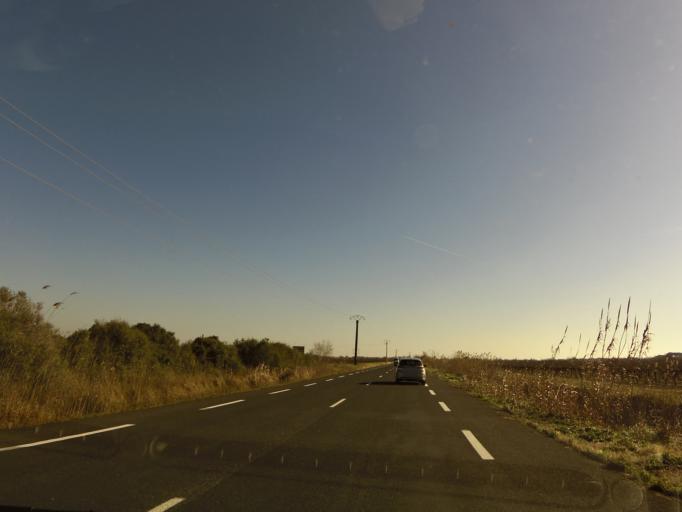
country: FR
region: Languedoc-Roussillon
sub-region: Departement du Gard
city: Aigues-Mortes
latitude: 43.5682
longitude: 4.3110
